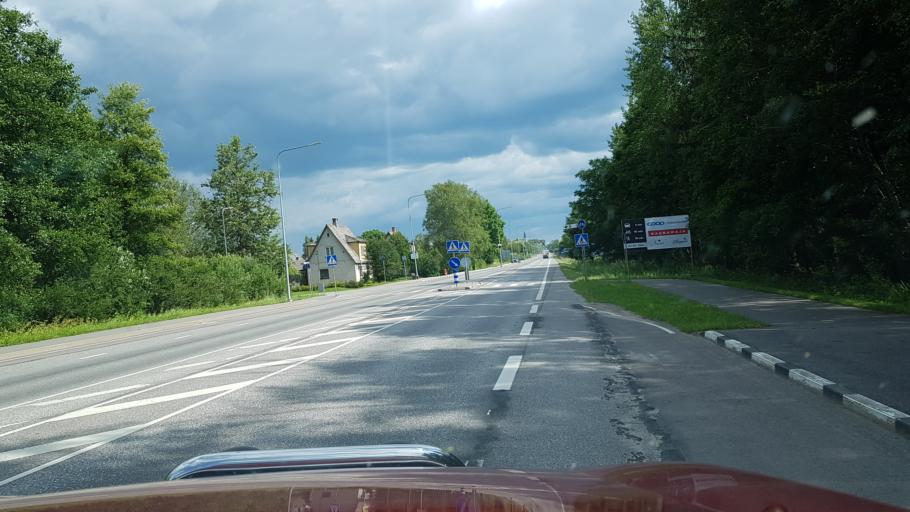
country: EE
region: Vorumaa
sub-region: Voru linn
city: Voru
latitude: 57.8566
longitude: 26.9778
